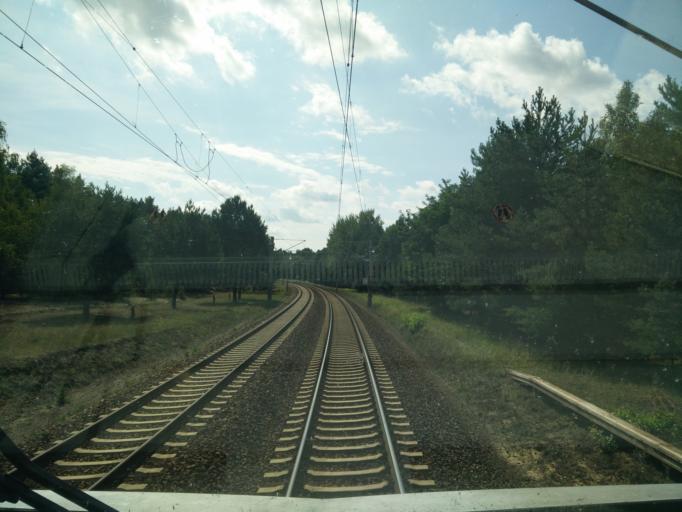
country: DE
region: Brandenburg
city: Schwerin
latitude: 52.1921
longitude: 13.6255
